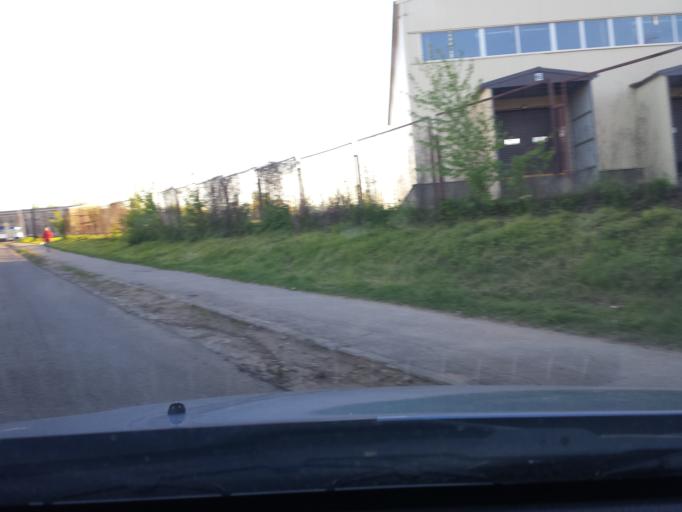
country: LV
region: Riga
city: Jaunciems
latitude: 57.0178
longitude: 24.1245
